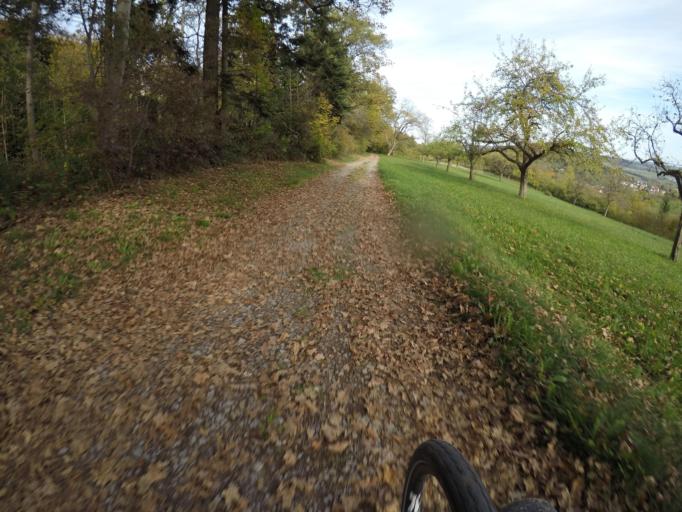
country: DE
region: Baden-Wuerttemberg
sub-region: Karlsruhe Region
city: Simmozheim
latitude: 48.7751
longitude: 8.8031
